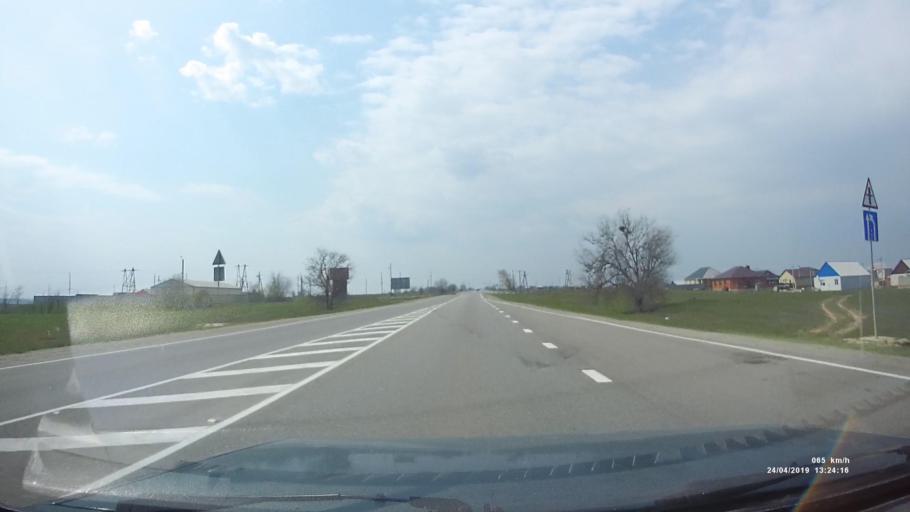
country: RU
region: Kalmykiya
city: Elista
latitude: 46.2844
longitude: 44.2580
